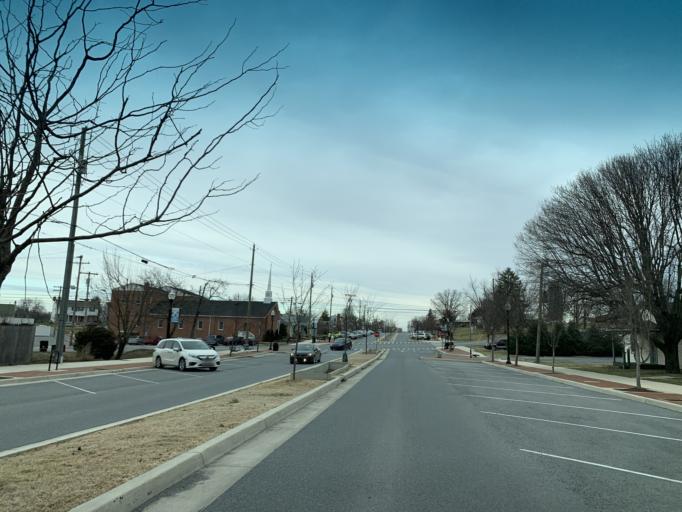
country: US
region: West Virginia
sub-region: Jefferson County
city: Ranson
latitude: 39.2956
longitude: -77.8603
